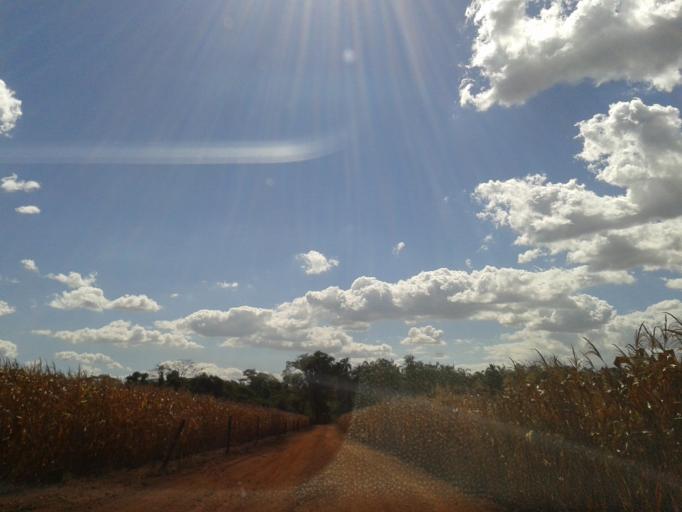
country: BR
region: Minas Gerais
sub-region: Capinopolis
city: Capinopolis
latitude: -18.6202
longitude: -49.4739
